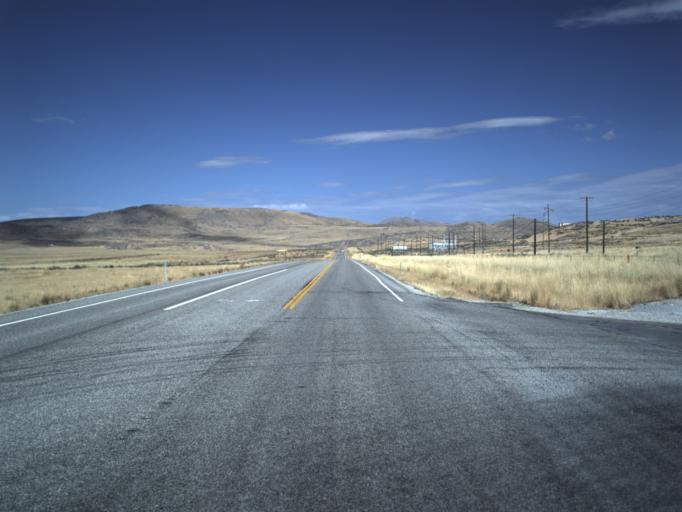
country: US
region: Utah
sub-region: Box Elder County
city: Tremonton
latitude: 41.6388
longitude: -112.4258
